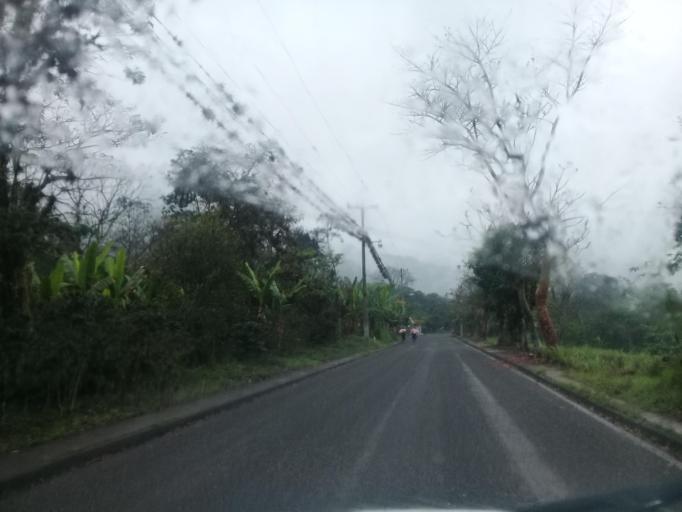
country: MX
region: Veracruz
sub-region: Amatlan de los Reyes
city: Centro de Readaptacion Social
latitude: 18.8011
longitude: -96.9472
